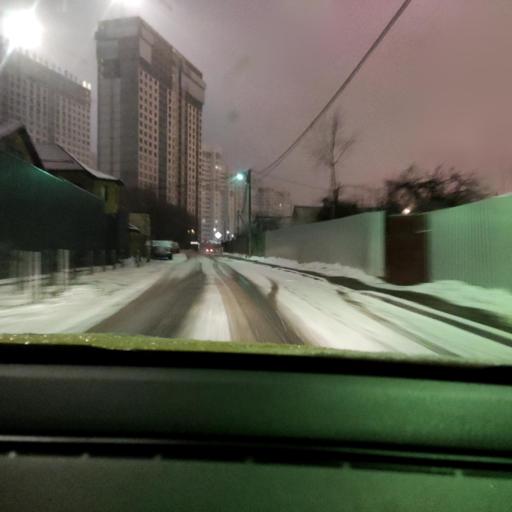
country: RU
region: Moskovskaya
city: Marfino
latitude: 55.7046
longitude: 37.3831
